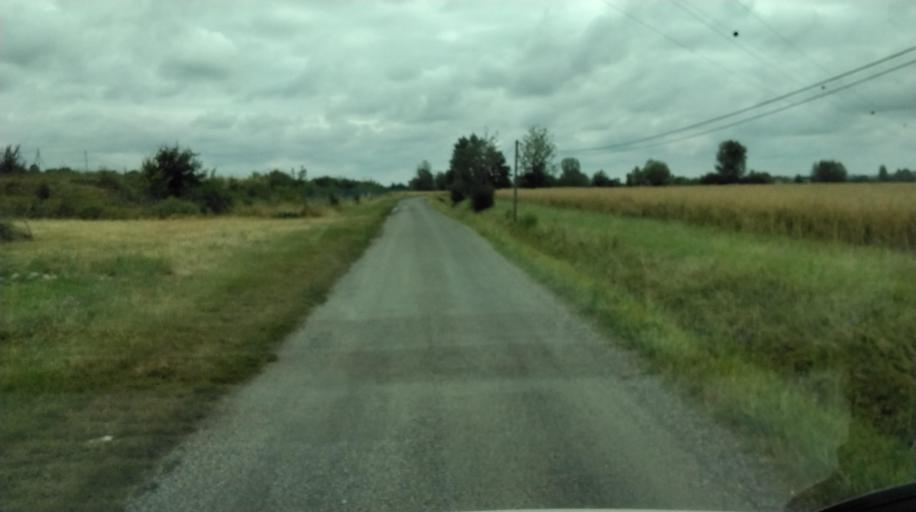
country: FR
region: Midi-Pyrenees
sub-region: Departement de la Haute-Garonne
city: Martres-Tolosane
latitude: 43.2047
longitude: 1.0333
